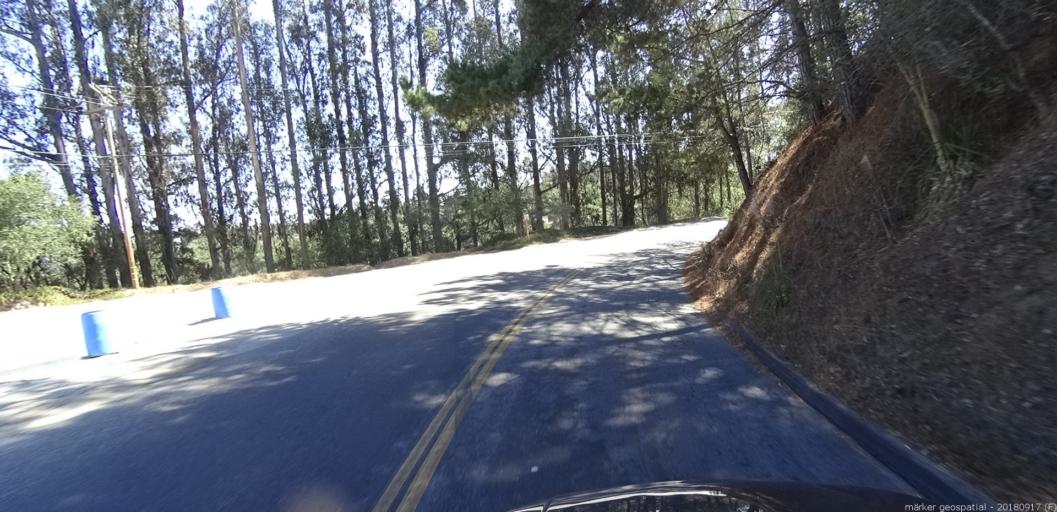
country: US
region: California
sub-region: Monterey County
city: Prunedale
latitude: 36.8319
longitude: -121.6810
